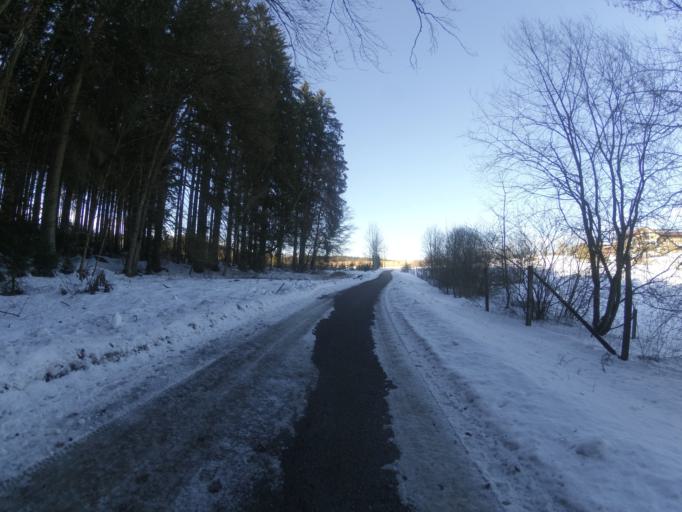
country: DE
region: Bavaria
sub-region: Upper Bavaria
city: Feldkirchen-Westerham
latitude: 47.9278
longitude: 11.8125
